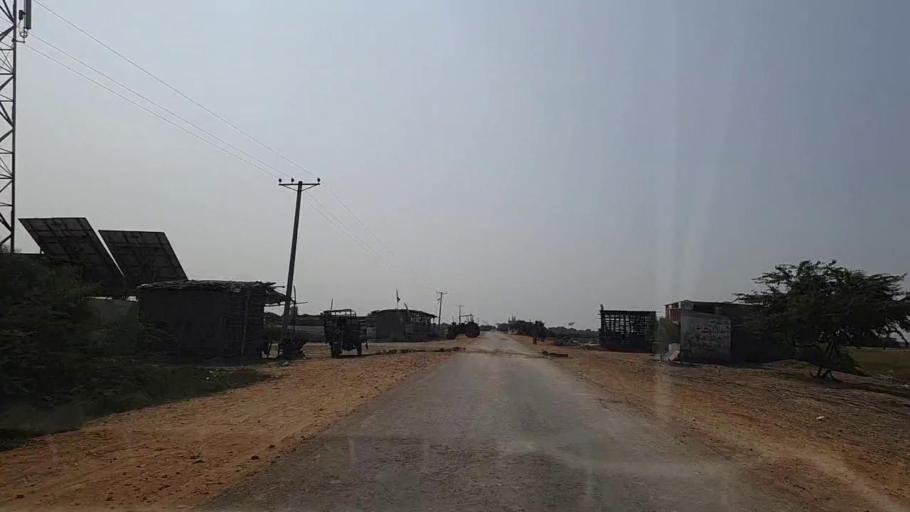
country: PK
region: Sindh
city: Chuhar Jamali
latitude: 24.2837
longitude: 67.9215
